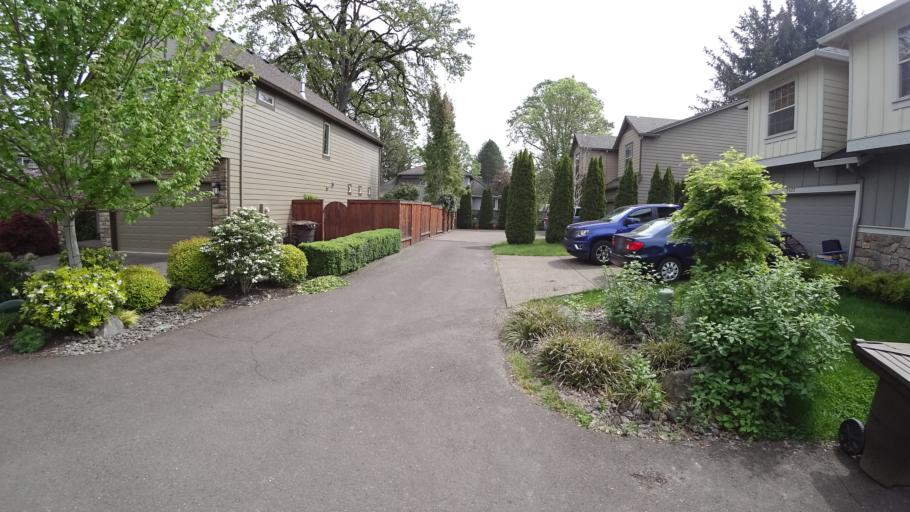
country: US
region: Oregon
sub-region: Washington County
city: Hillsboro
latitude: 45.5458
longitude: -122.9977
